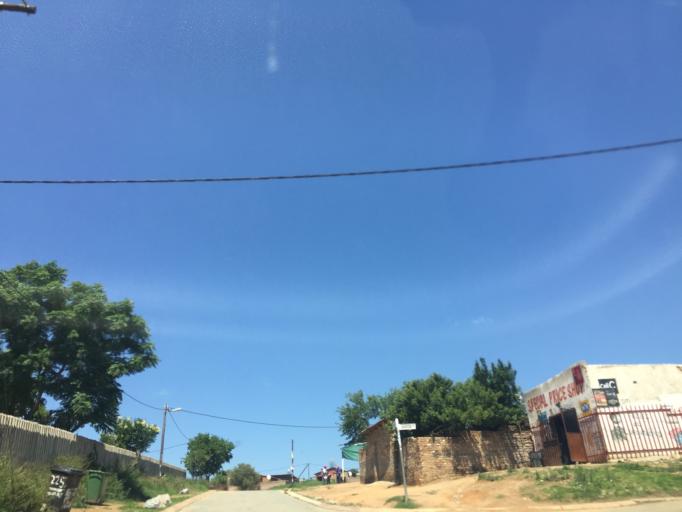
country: ZA
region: Gauteng
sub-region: West Rand District Municipality
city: Muldersdriseloop
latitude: -26.0182
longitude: 27.9284
